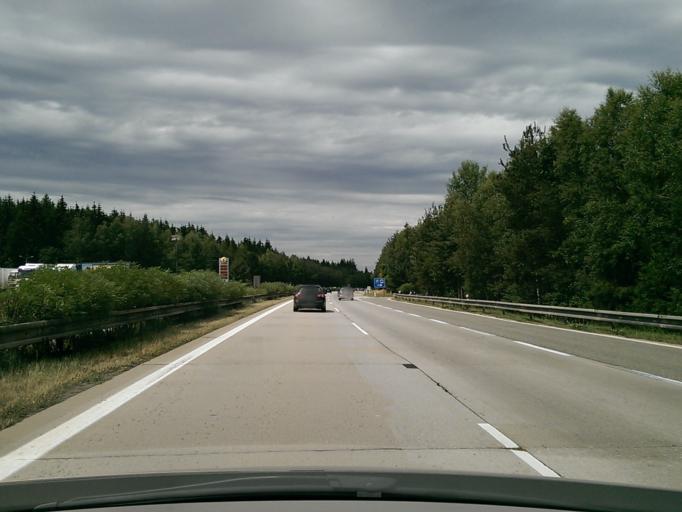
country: CZ
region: Vysocina
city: Luka nad Jihlavou
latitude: 49.4121
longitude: 15.7219
